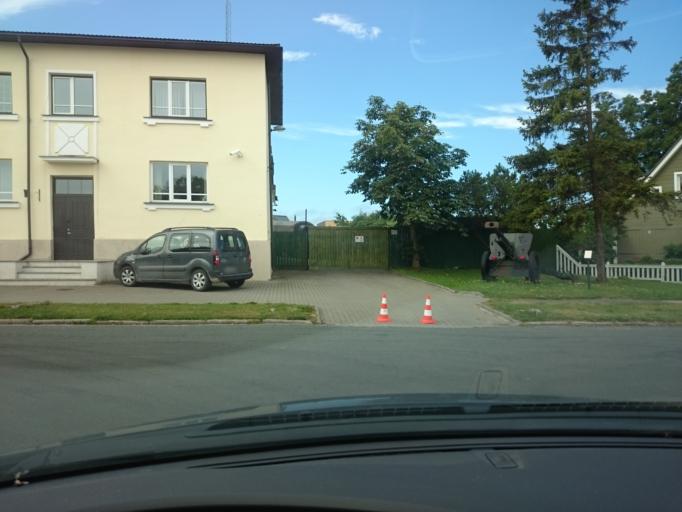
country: EE
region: Laeaene
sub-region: Haapsalu linn
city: Haapsalu
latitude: 58.9485
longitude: 23.5292
